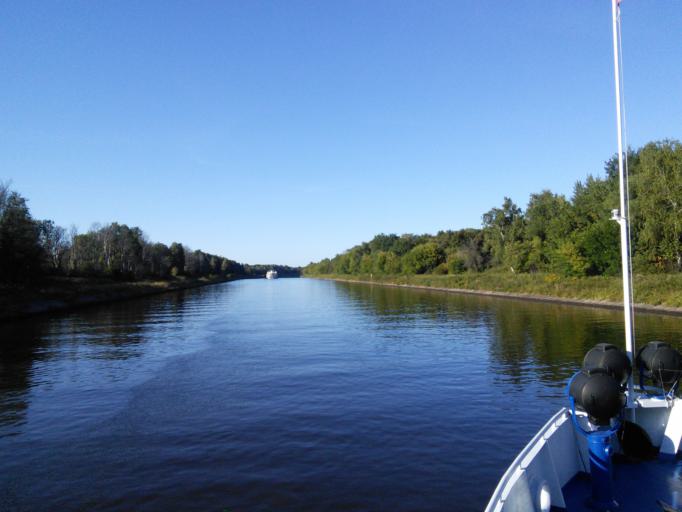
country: RU
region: Moskovskaya
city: Yakhroma
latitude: 56.3070
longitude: 37.4894
